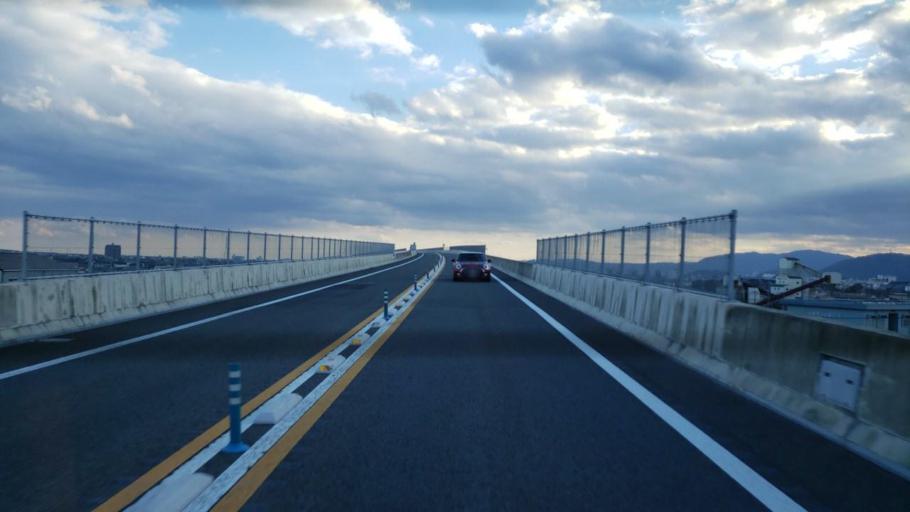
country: JP
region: Tokushima
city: Tokushima-shi
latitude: 34.1289
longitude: 134.5649
